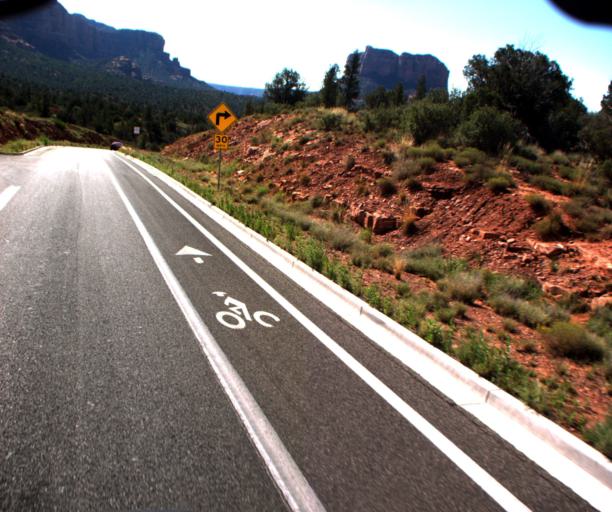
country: US
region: Arizona
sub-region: Yavapai County
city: Village of Oak Creek (Big Park)
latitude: 34.8232
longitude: -111.7764
